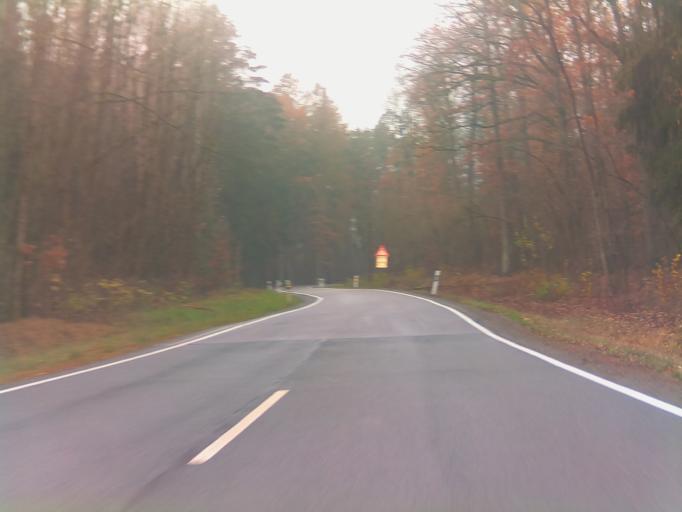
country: DE
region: Bavaria
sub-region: Regierungsbezirk Unterfranken
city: Hochheim
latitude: 50.4016
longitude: 10.4610
